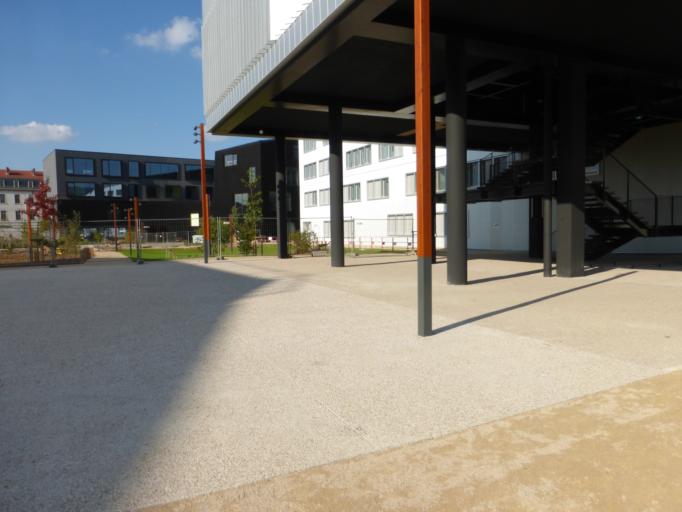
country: FR
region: Lorraine
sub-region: Departement de Meurthe-et-Moselle
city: Nancy
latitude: 48.6736
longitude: 6.1699
